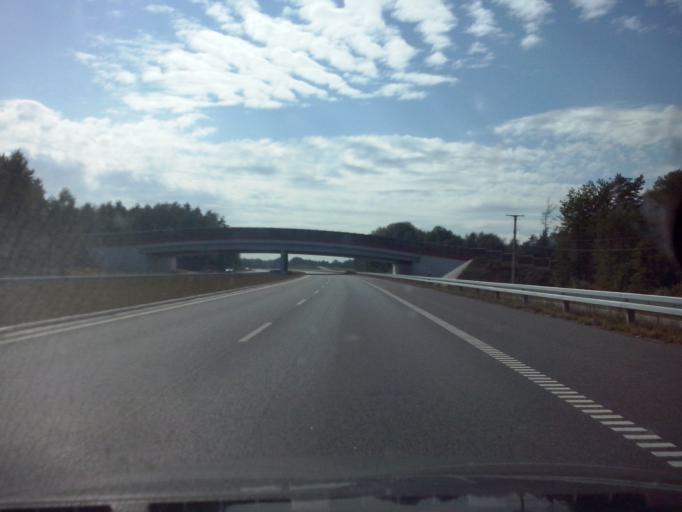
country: PL
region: Lesser Poland Voivodeship
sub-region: Powiat tarnowski
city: Jodlowka-Walki
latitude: 50.0951
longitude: 21.1684
